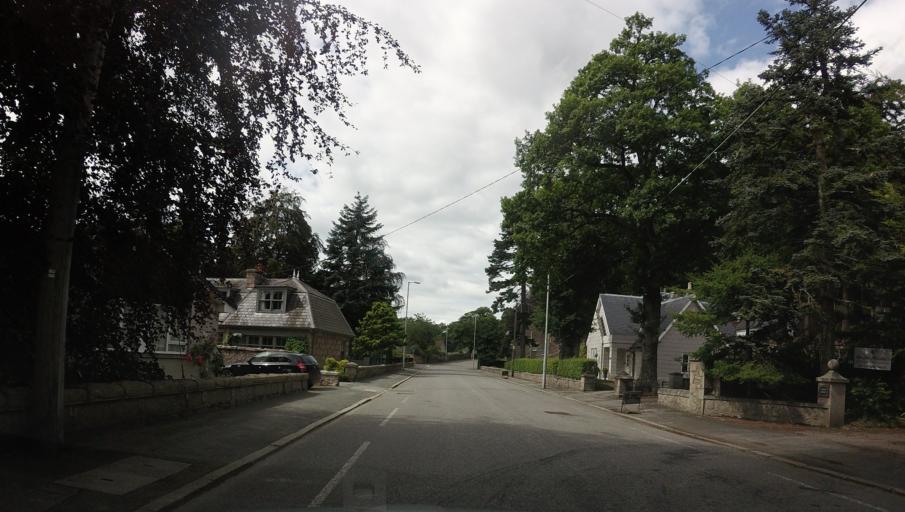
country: GB
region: Scotland
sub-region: Aberdeenshire
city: Ballater
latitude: 57.0507
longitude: -3.0493
